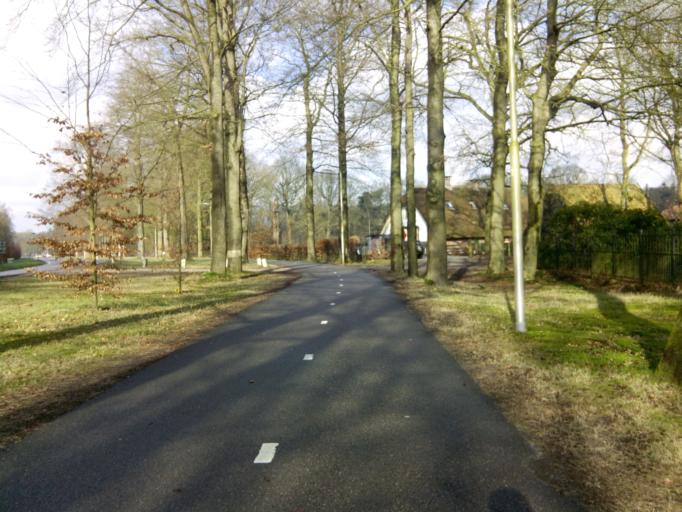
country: NL
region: Utrecht
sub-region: Gemeente Utrechtse Heuvelrug
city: Maarsbergen
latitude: 52.0443
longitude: 5.4096
